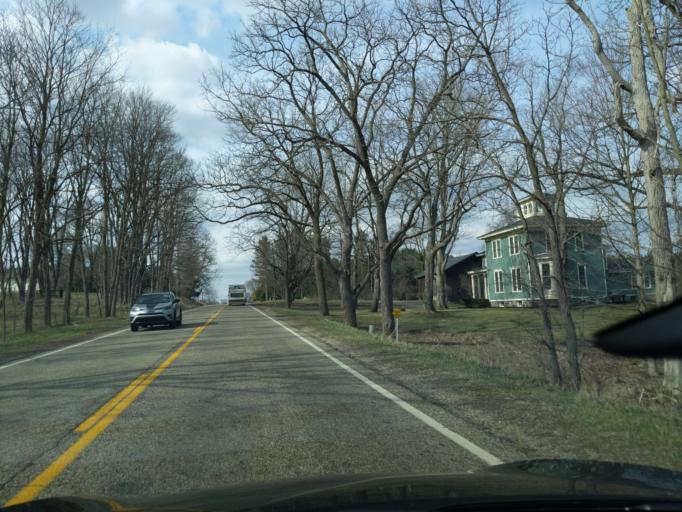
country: US
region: Michigan
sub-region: Jackson County
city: Jackson
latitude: 42.3463
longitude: -84.4149
